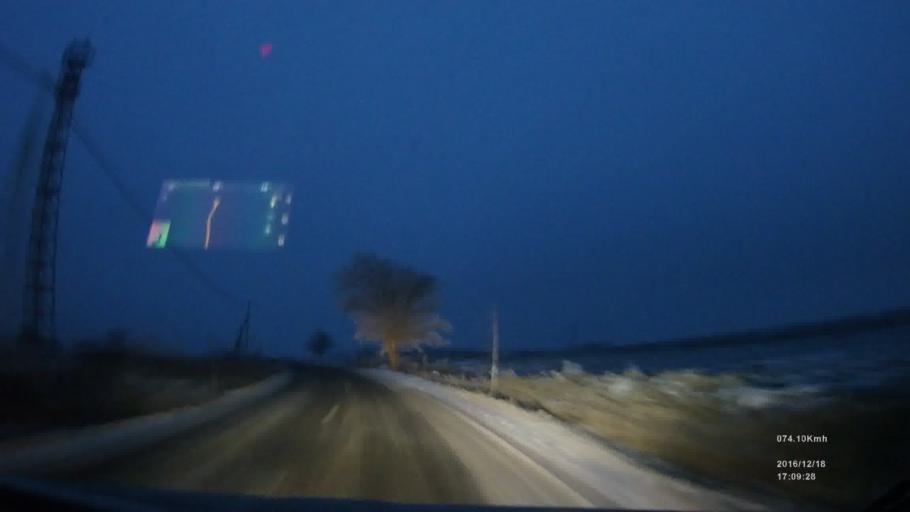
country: SK
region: Presovsky
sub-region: Okres Presov
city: Presov
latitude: 48.8732
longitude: 21.3109
